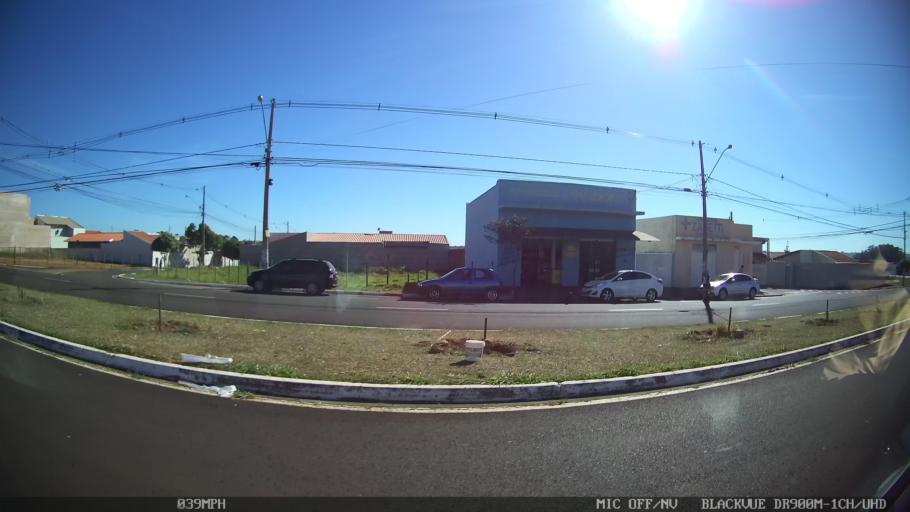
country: BR
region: Sao Paulo
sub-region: Franca
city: Franca
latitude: -20.5644
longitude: -47.3505
